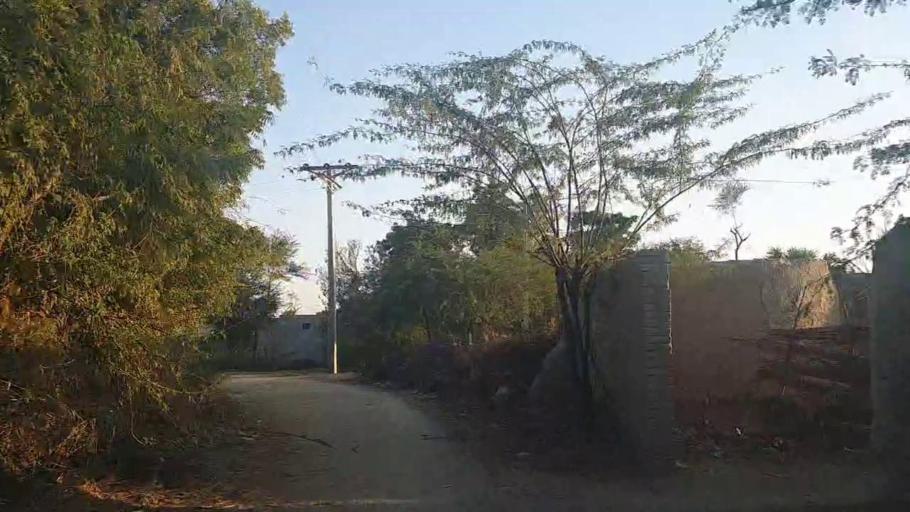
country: PK
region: Sindh
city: Jam Sahib
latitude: 26.3204
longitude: 68.7027
